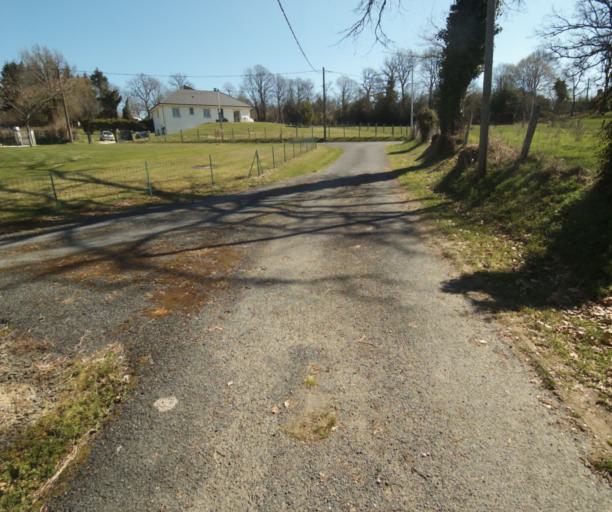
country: FR
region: Limousin
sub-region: Departement de la Correze
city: Saint-Clement
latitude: 45.3247
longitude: 1.6489
